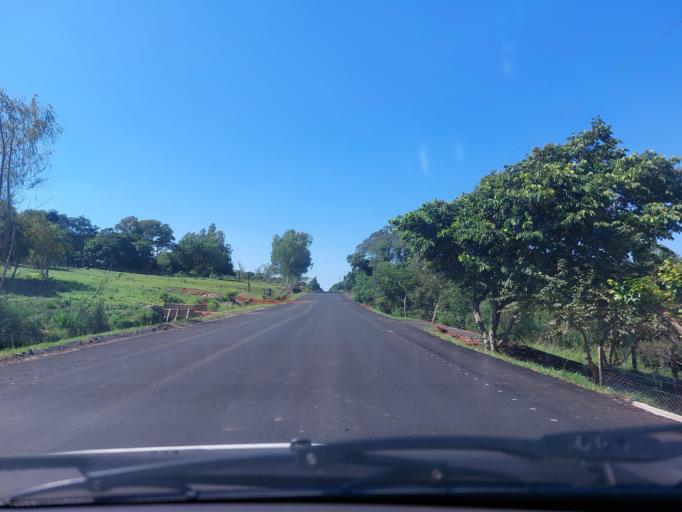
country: PY
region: San Pedro
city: Guayaybi
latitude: -24.5503
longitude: -56.5089
